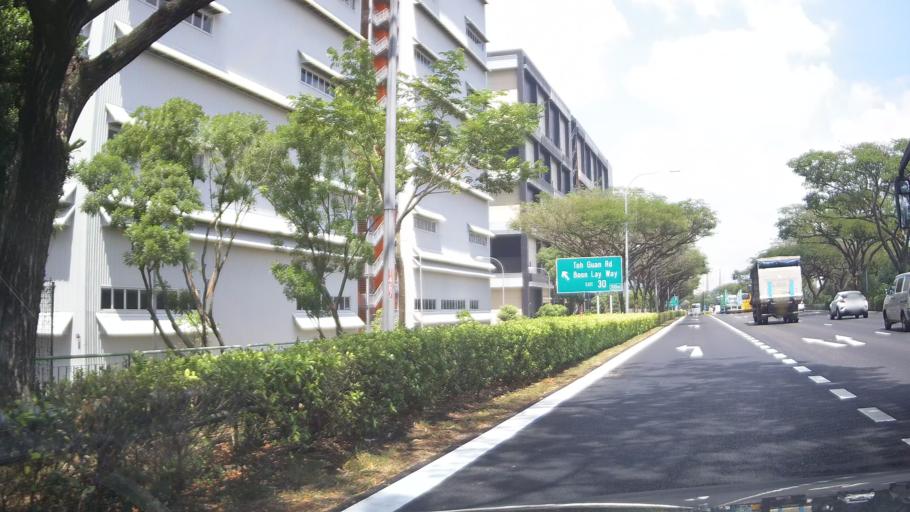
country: SG
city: Singapore
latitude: 1.3391
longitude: 103.7529
